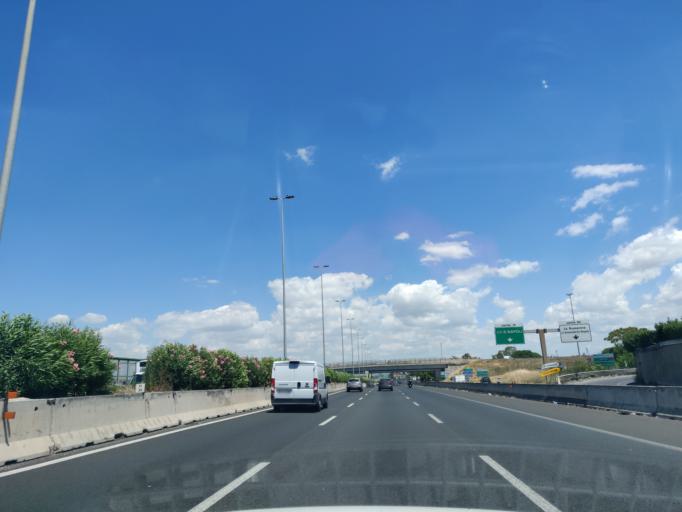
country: IT
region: Latium
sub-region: Citta metropolitana di Roma Capitale
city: Ciampino
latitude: 41.8510
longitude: 12.5968
